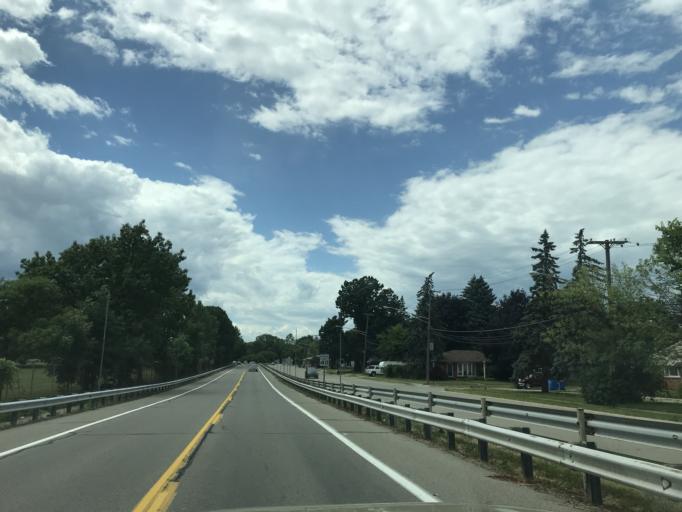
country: US
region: Michigan
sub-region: Wayne County
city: Dearborn Heights
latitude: 42.3514
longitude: -83.2938
